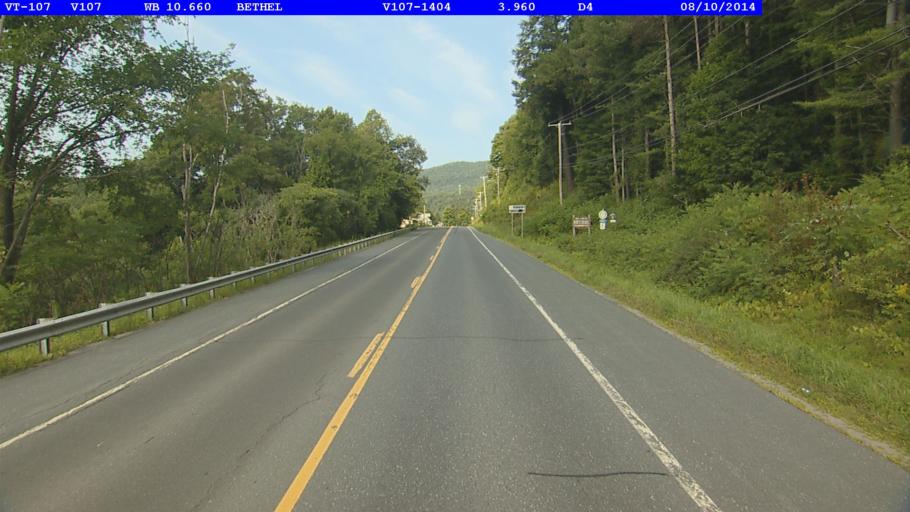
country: US
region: Vermont
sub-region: Orange County
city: Randolph
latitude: 43.8256
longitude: -72.6209
